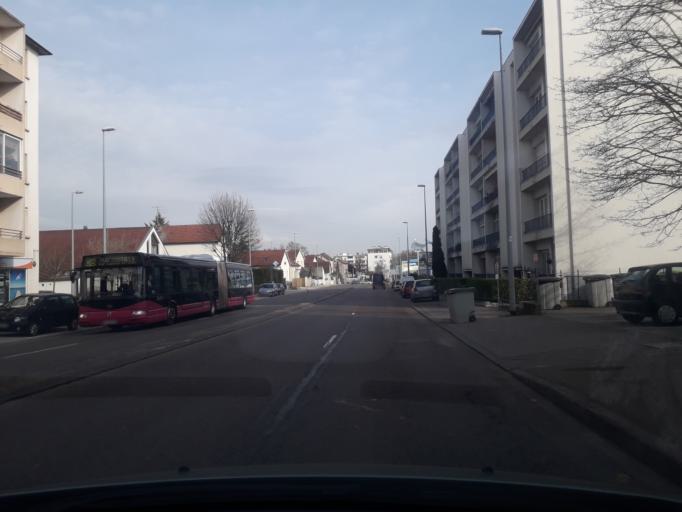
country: FR
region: Bourgogne
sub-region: Departement de la Cote-d'Or
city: Talant
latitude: 47.3321
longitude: 5.0147
